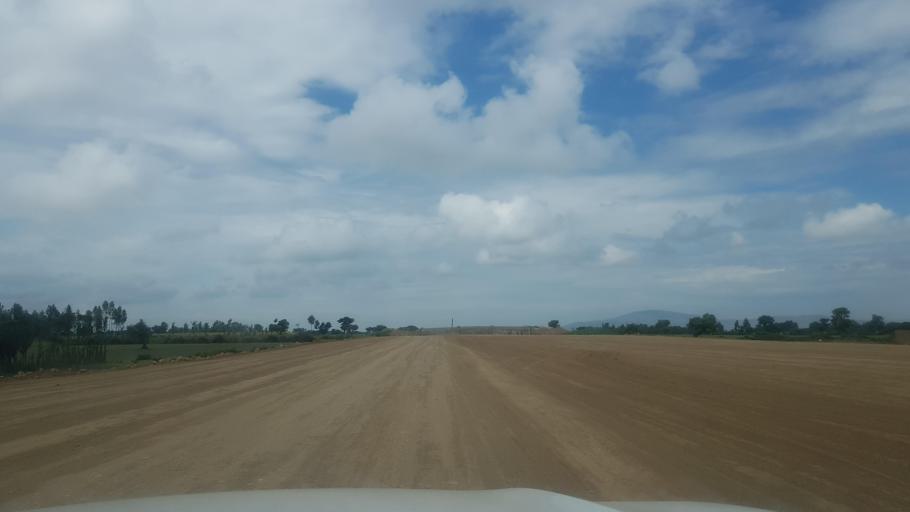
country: ET
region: Oromiya
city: Shashemene
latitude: 7.2404
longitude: 38.5802
